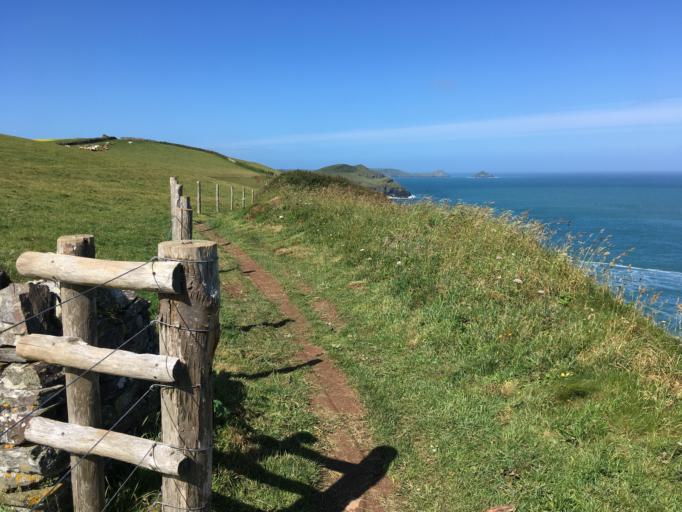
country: GB
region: England
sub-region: Cornwall
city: Polzeath
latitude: 50.5968
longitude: -4.8502
